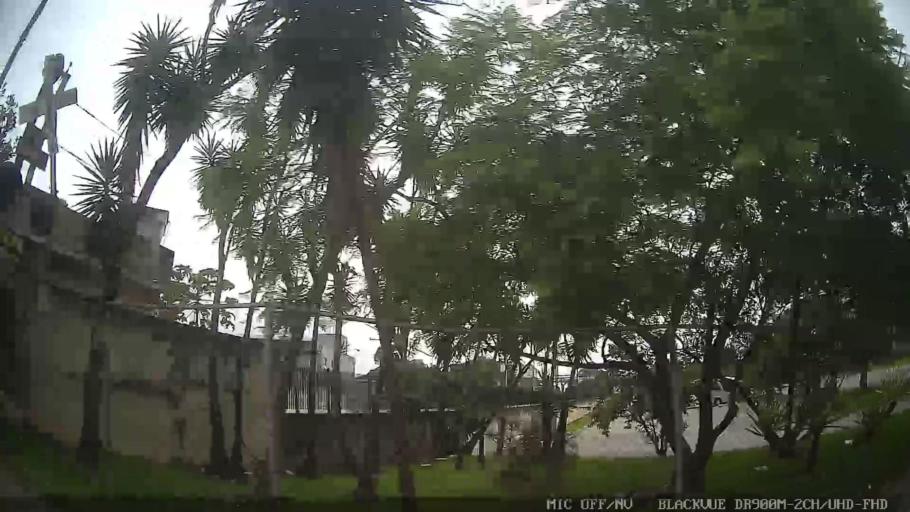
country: BR
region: Sao Paulo
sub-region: Mogi das Cruzes
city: Mogi das Cruzes
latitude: -23.5141
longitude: -46.1851
